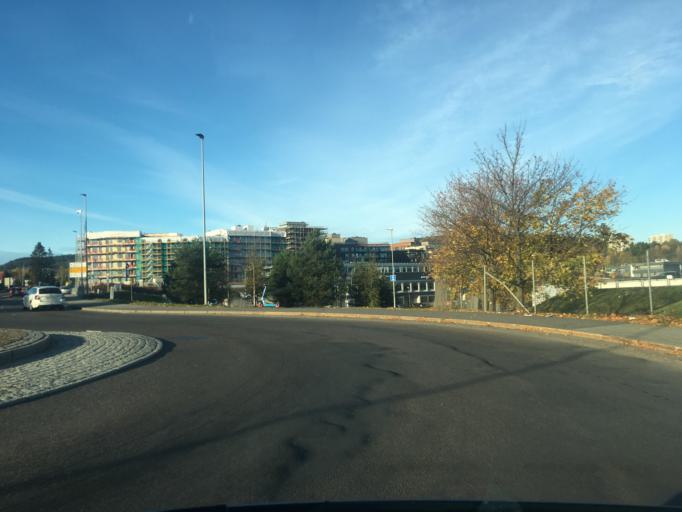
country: NO
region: Oslo
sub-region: Oslo
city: Oslo
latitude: 59.9323
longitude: 10.8293
